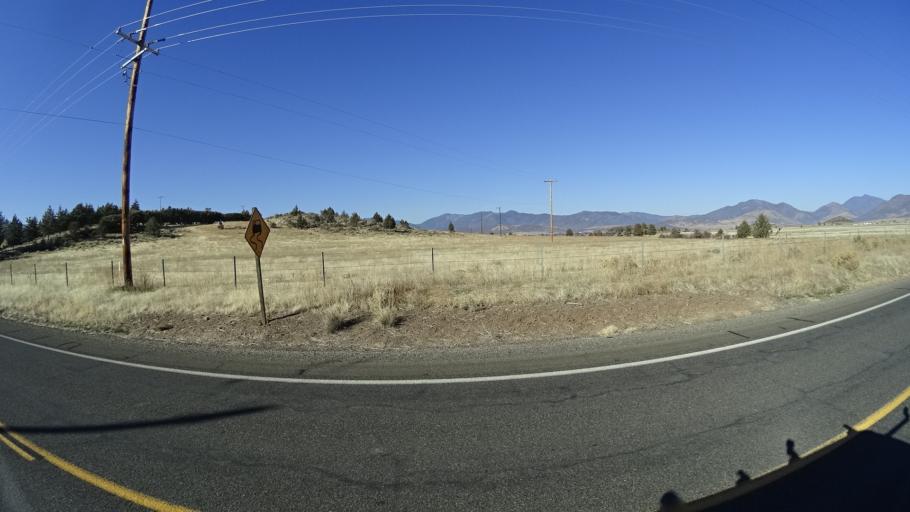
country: US
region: California
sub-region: Siskiyou County
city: Montague
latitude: 41.7134
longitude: -122.5364
